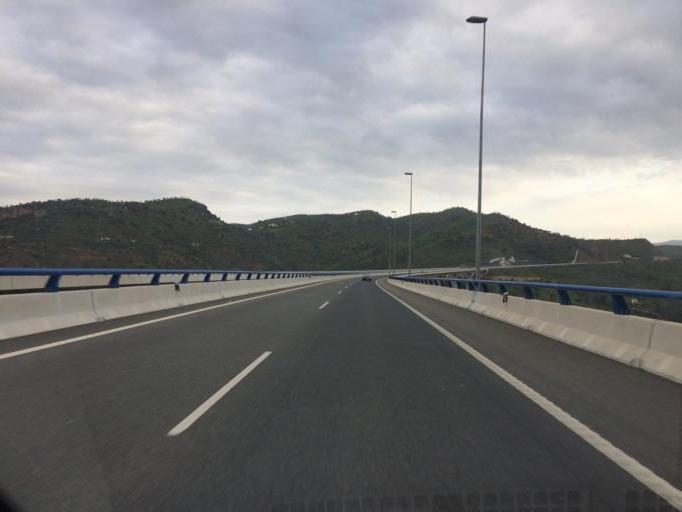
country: ES
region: Andalusia
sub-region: Provincia de Malaga
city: Casabermeja
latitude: 36.8712
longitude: -4.4831
